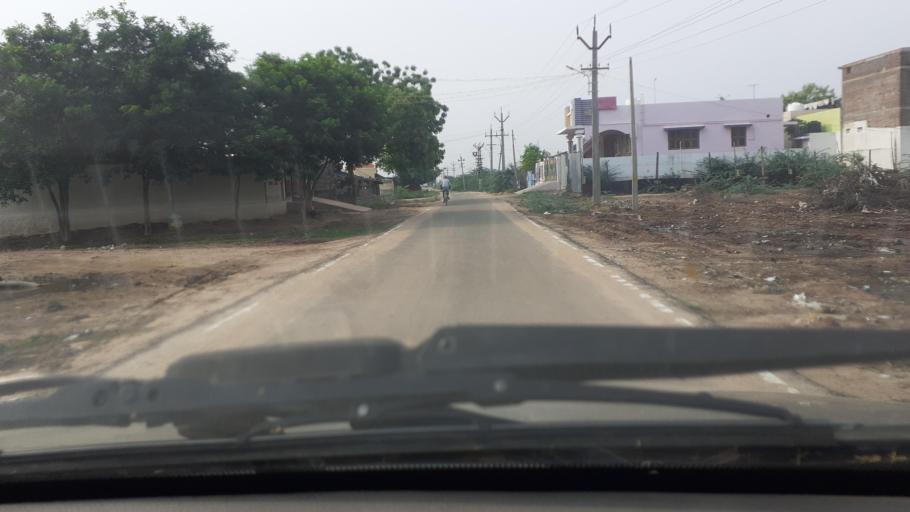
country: IN
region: Tamil Nadu
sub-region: Thoothukkudi
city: Korampallam
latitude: 8.7964
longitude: 78.1056
